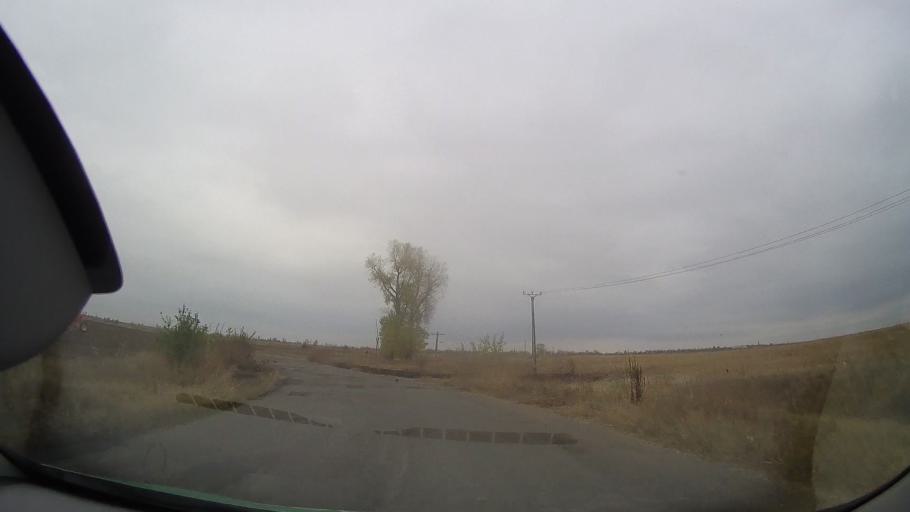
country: RO
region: Braila
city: Dudesti
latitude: 44.9342
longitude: 27.4267
